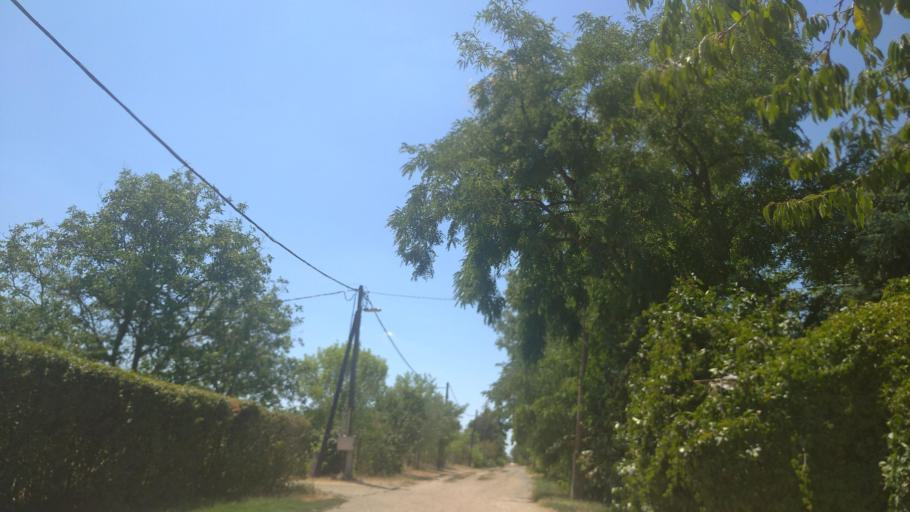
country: HU
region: Bekes
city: Oroshaza
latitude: 46.5571
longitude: 20.6246
